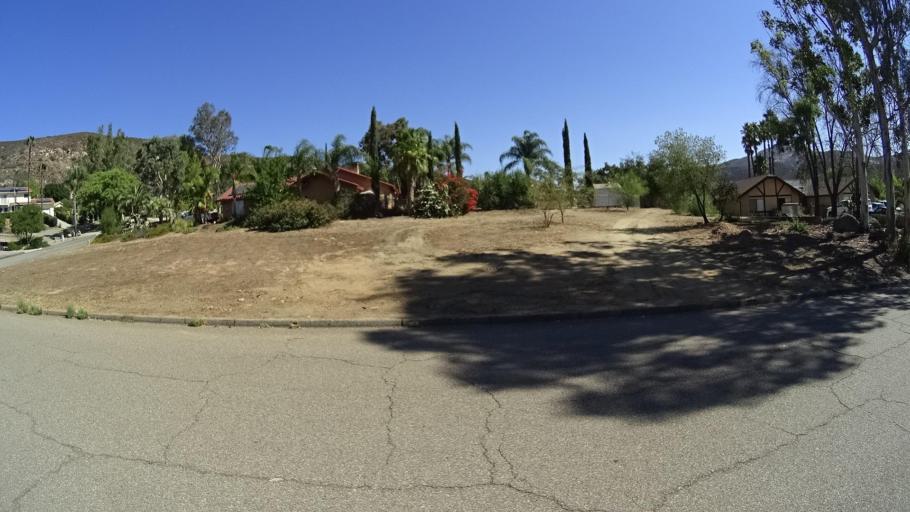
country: US
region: California
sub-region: San Diego County
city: San Diego Country Estates
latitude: 33.0256
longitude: -116.8047
